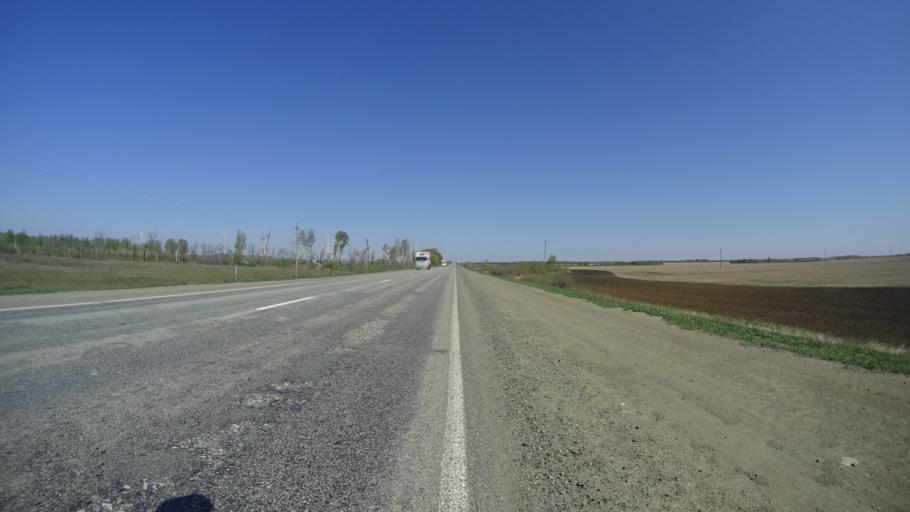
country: RU
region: Chelyabinsk
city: Troitsk
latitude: 54.1938
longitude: 61.4331
